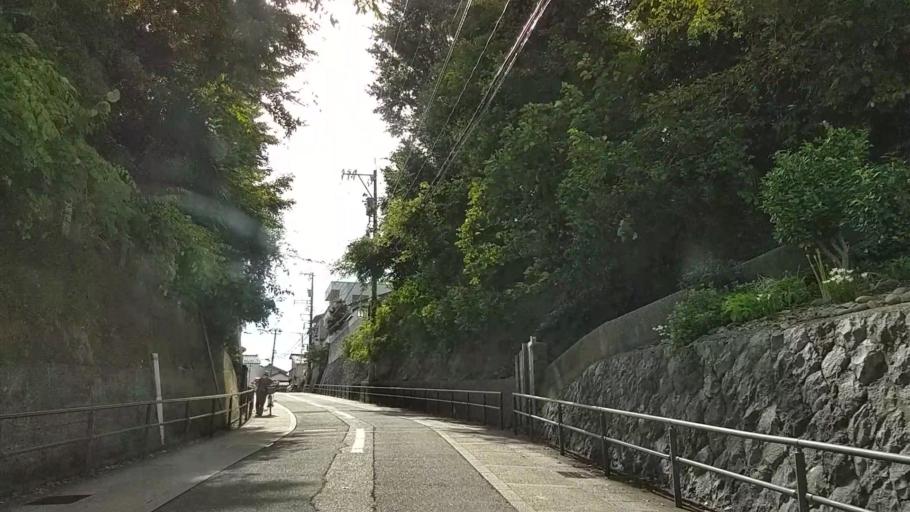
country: JP
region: Ishikawa
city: Nonoichi
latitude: 36.5466
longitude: 136.6608
